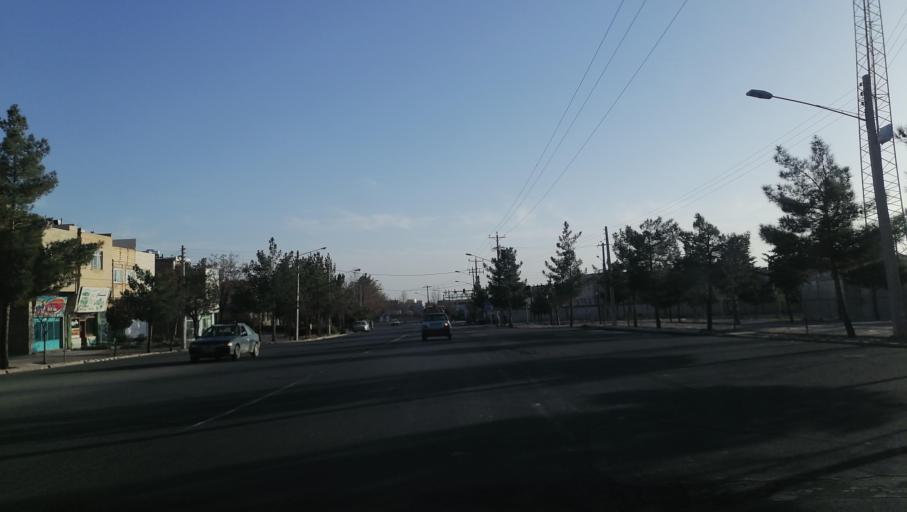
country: IR
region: Razavi Khorasan
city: Sabzevar
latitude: 36.2798
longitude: 57.6753
